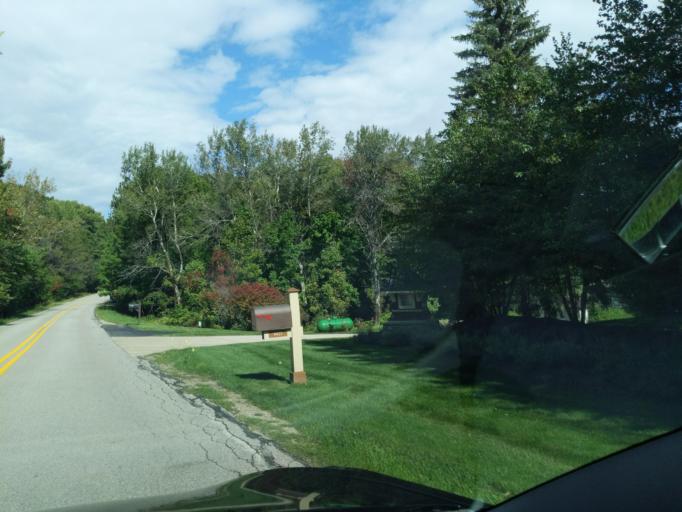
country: US
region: Michigan
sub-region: Antrim County
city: Bellaire
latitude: 44.9689
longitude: -85.3237
